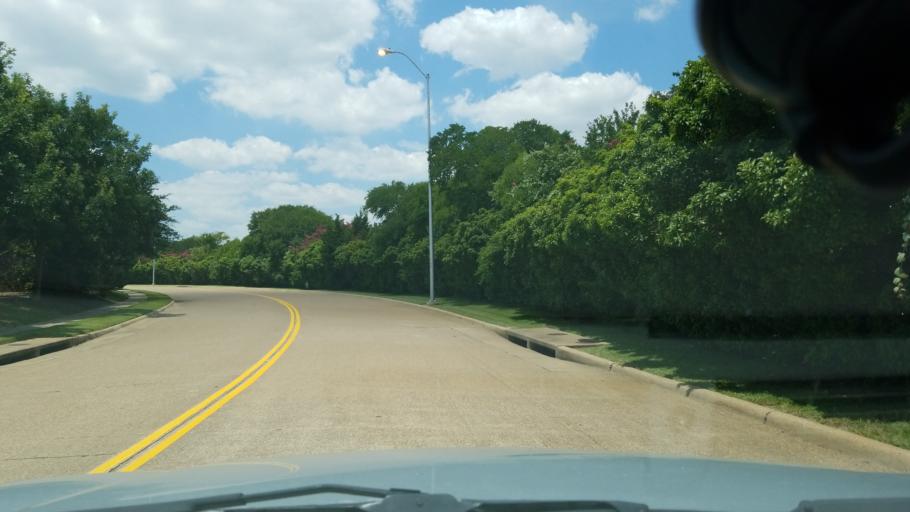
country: US
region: Texas
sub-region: Dallas County
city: Duncanville
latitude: 32.6826
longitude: -96.8804
